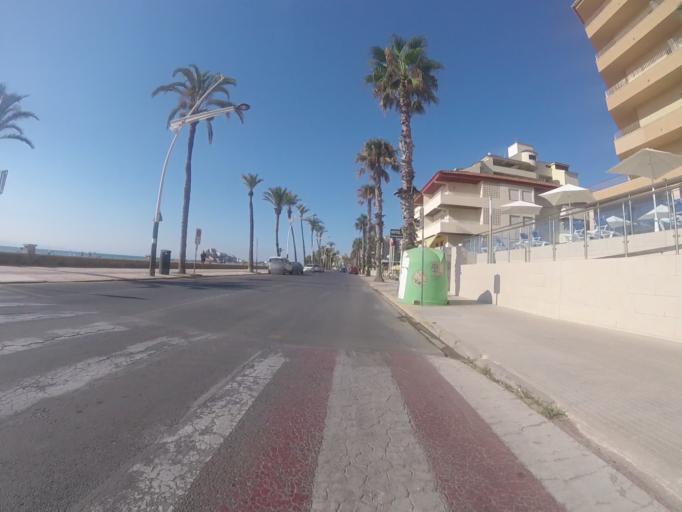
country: ES
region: Valencia
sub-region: Provincia de Castello
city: Peniscola
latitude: 40.3732
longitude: 0.4057
